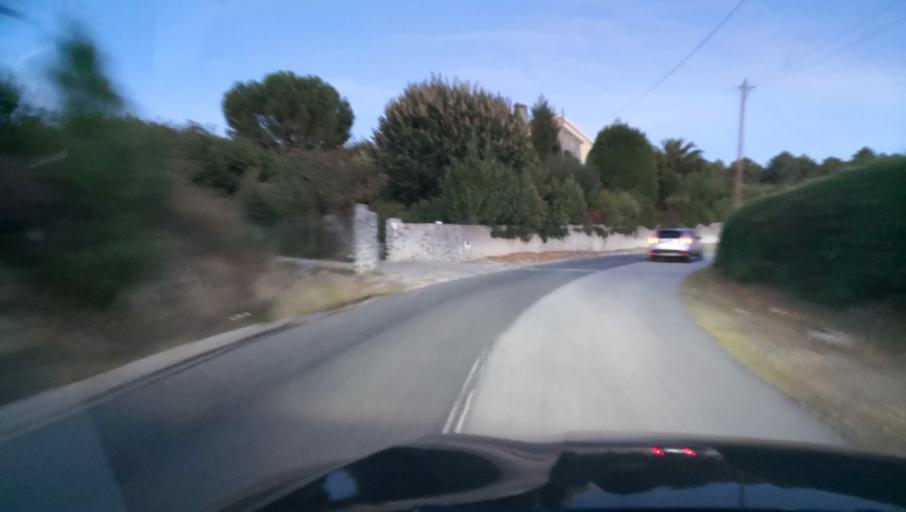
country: PT
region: Vila Real
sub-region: Sabrosa
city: Sabrosa
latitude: 41.2582
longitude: -7.5830
